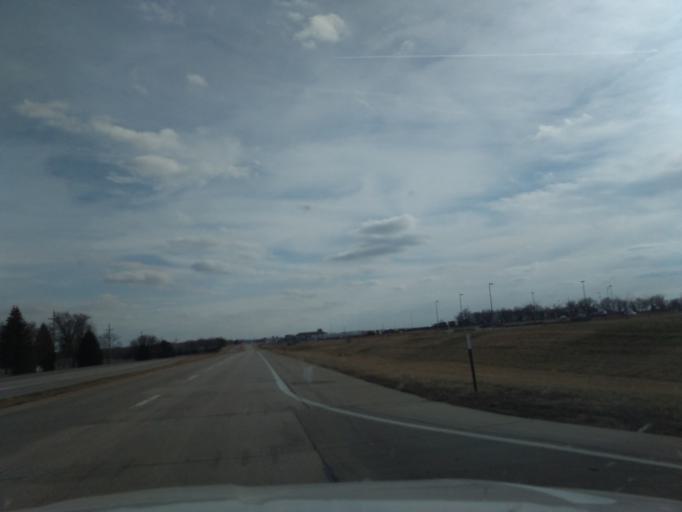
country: US
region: Nebraska
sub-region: Gage County
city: Beatrice
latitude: 40.3176
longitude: -96.7471
